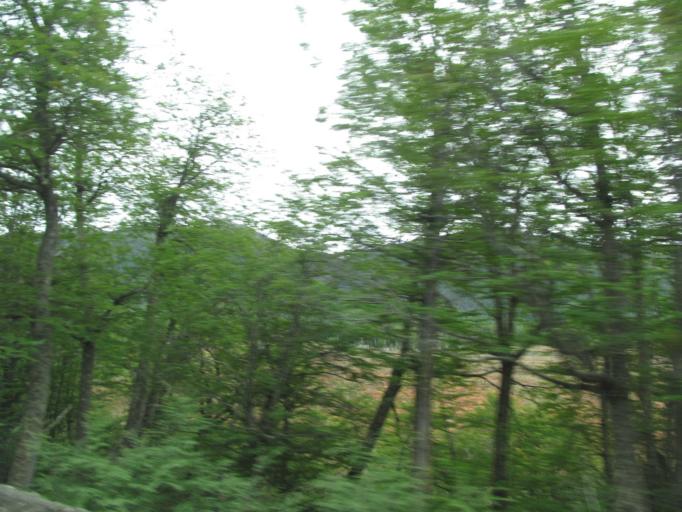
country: AR
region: Tierra del Fuego
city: Ushuaia
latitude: -54.7570
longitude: -67.7892
